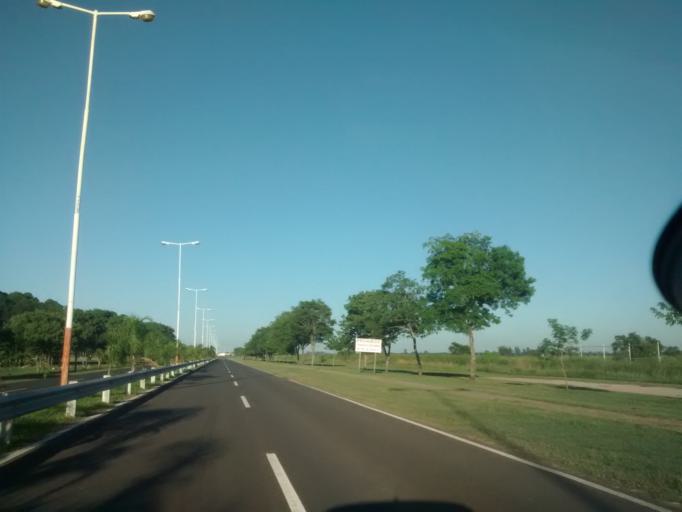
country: AR
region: Chaco
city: Fontana
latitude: -27.4409
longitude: -59.0337
